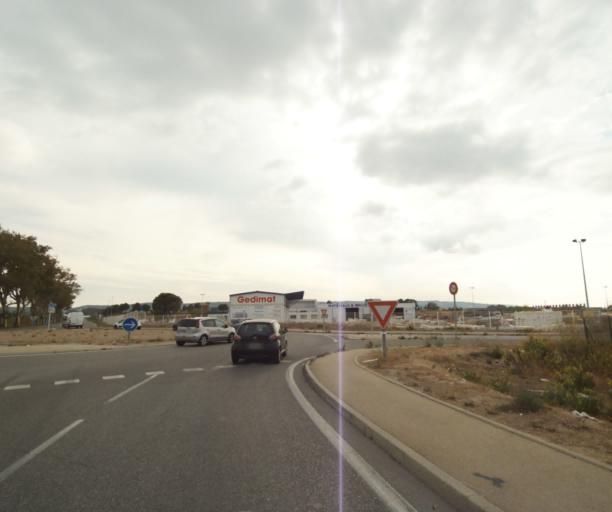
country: FR
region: Provence-Alpes-Cote d'Azur
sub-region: Departement des Bouches-du-Rhone
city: Marignane
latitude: 43.4018
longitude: 5.2010
